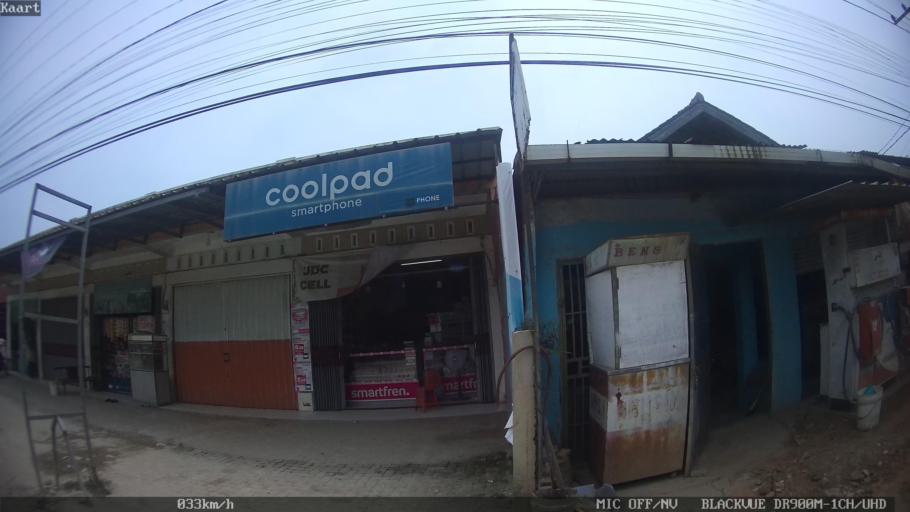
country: ID
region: Lampung
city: Bandarlampung
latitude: -5.4063
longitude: 105.3028
